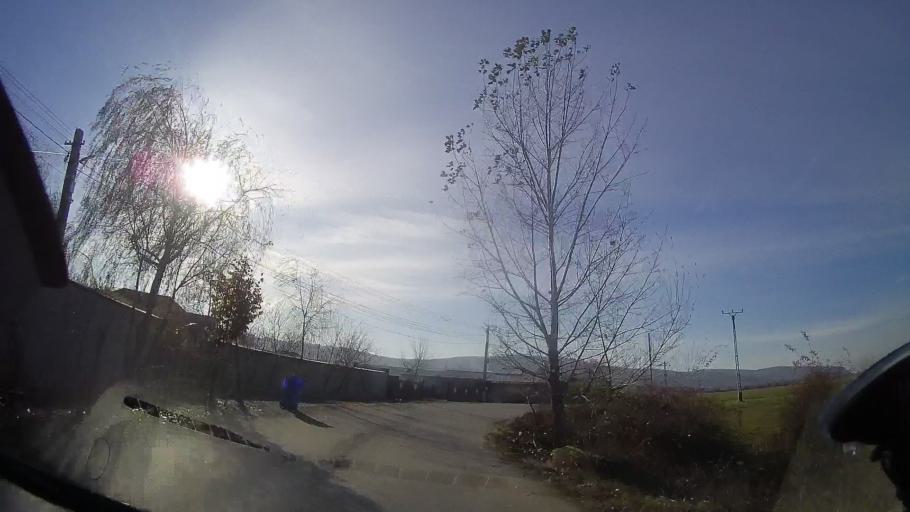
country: RO
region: Bihor
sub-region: Comuna Magesti
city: Magesti
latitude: 47.0184
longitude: 22.4674
